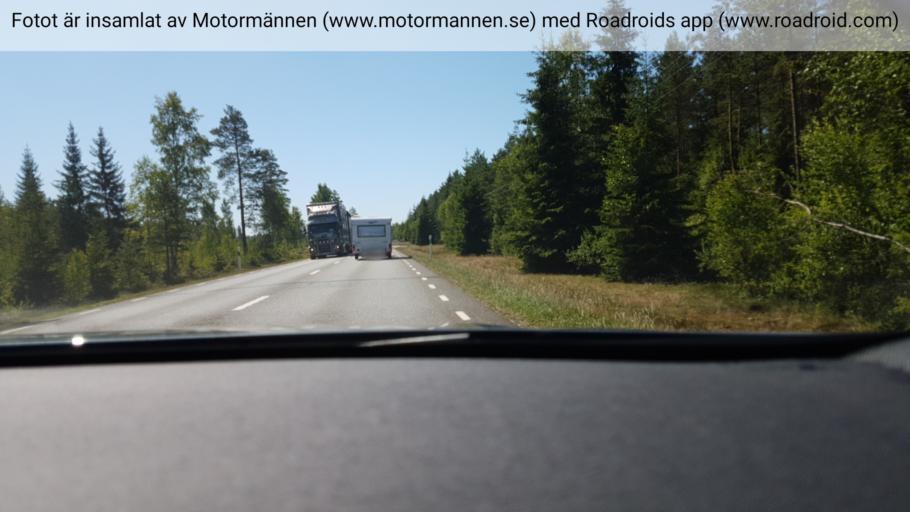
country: SE
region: Joenkoeping
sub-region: Gnosjo Kommun
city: Gnosjoe
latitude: 57.4668
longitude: 13.6514
